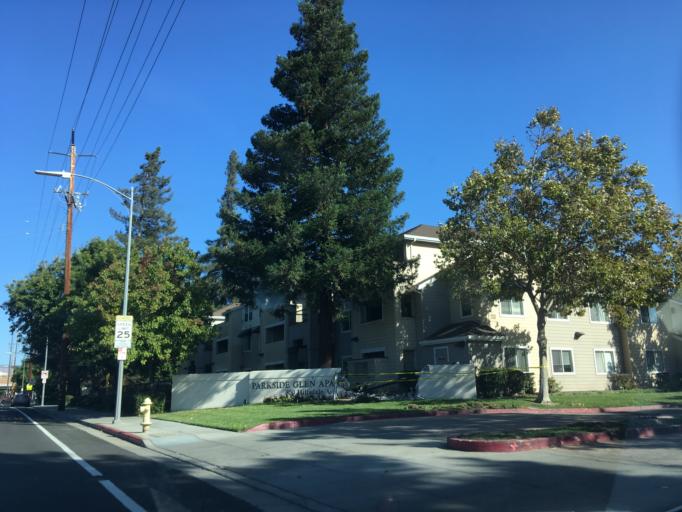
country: US
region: California
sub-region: Santa Clara County
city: Seven Trees
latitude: 37.2788
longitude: -121.8688
